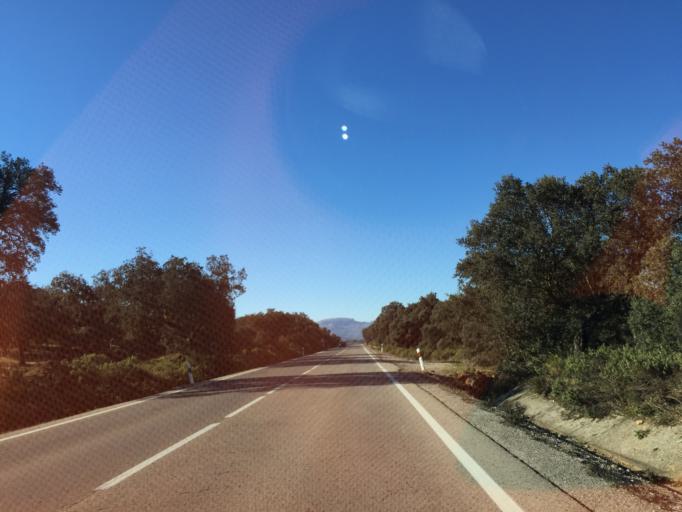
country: ES
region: Andalusia
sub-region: Provincia de Malaga
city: Arriate
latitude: 36.8211
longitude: -5.0968
